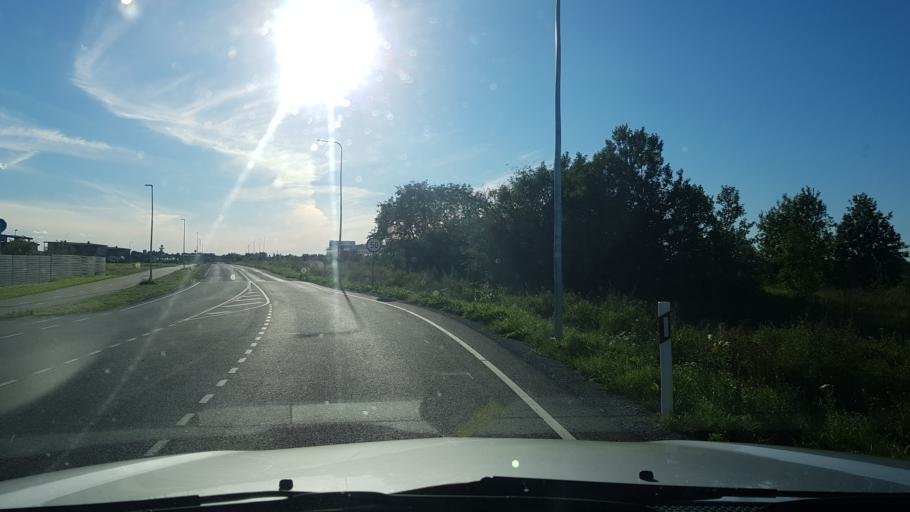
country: EE
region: Harju
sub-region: Rae vald
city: Jueri
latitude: 59.3874
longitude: 24.8502
